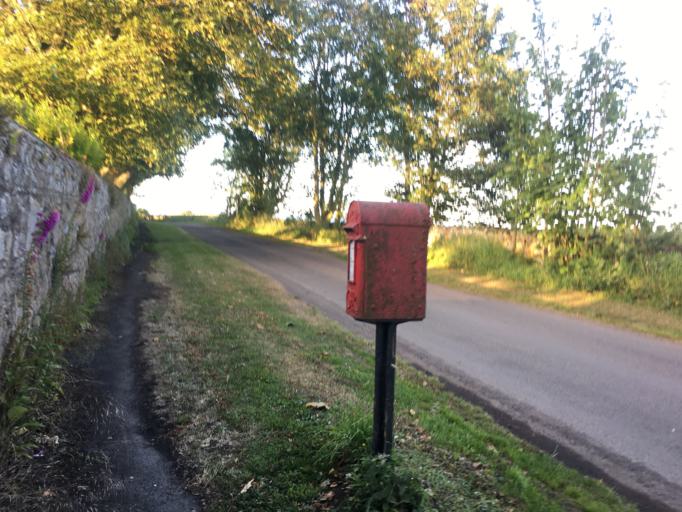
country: GB
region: England
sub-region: Northumberland
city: North Sunderland
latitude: 55.5867
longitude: -1.6776
